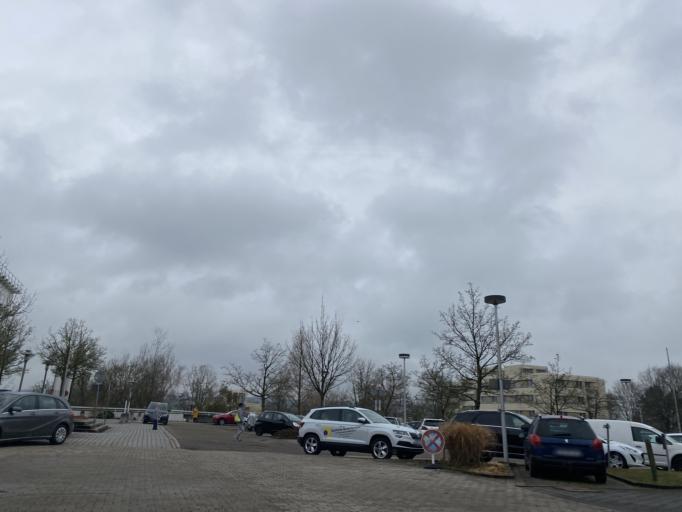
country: DE
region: Baden-Wuerttemberg
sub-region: Karlsruhe Region
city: Muhlacker
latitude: 48.9510
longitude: 8.8597
